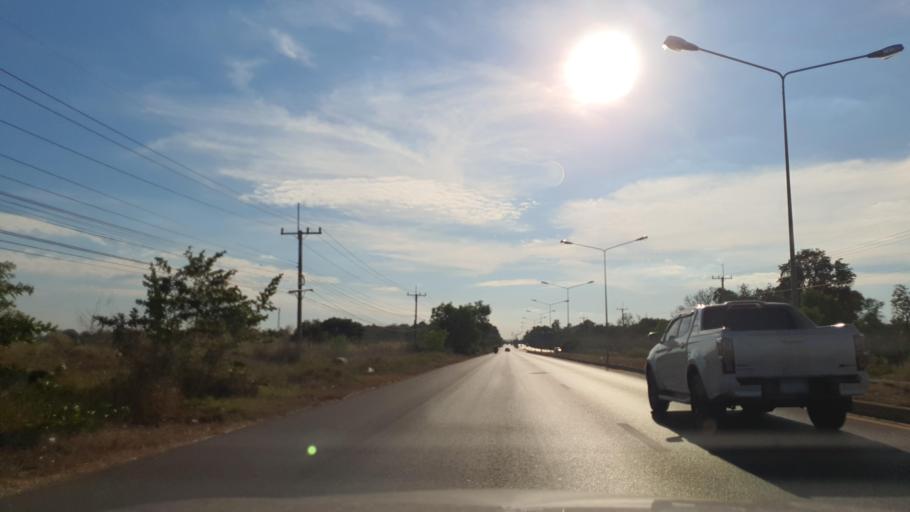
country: TH
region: Maha Sarakham
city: Kantharawichai
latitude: 16.3370
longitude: 103.3102
